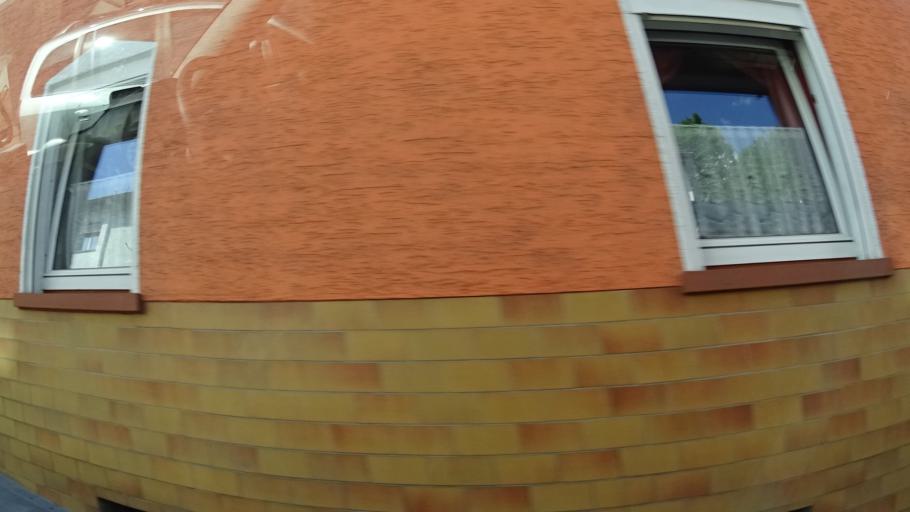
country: DE
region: Hesse
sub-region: Regierungsbezirk Darmstadt
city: Furth
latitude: 49.6377
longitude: 8.8338
